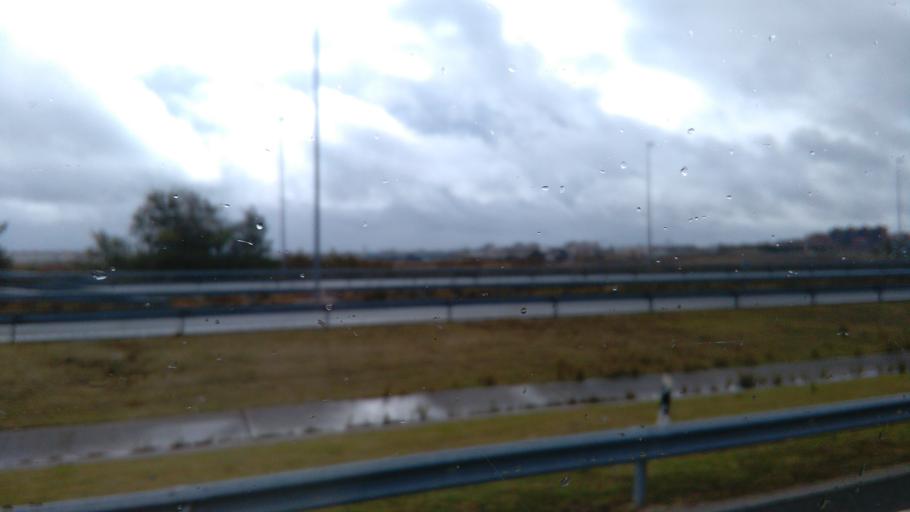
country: ES
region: Madrid
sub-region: Provincia de Madrid
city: Alcorcon
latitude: 40.3115
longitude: -3.8275
